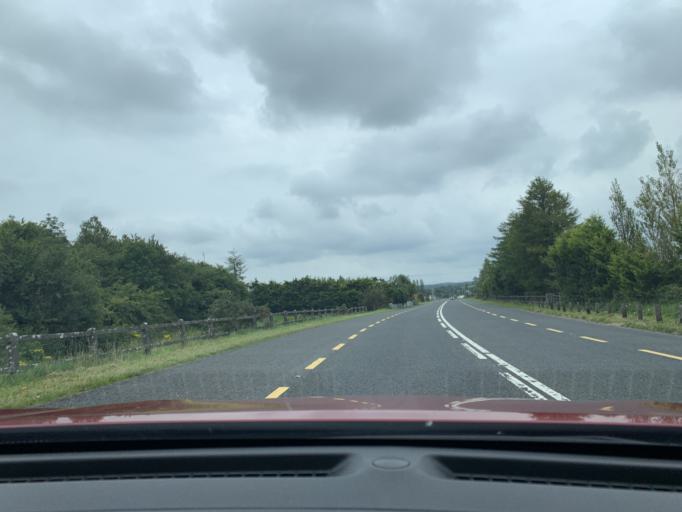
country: IE
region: Connaught
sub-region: Maigh Eo
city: Swinford
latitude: 53.8640
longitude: -8.8542
